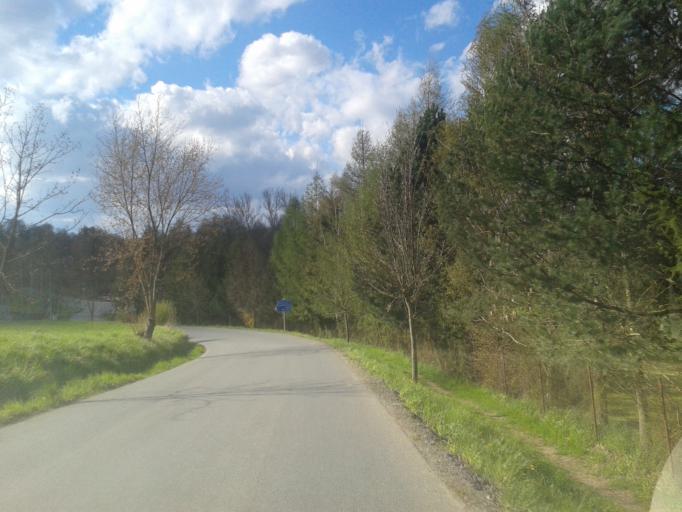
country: CZ
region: Central Bohemia
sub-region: Okres Beroun
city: Lodenice
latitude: 50.0096
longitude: 14.1506
